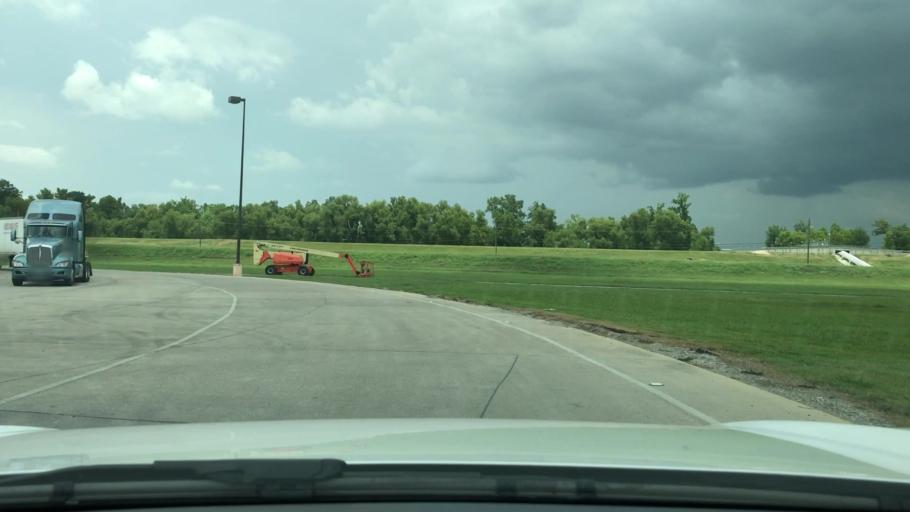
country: US
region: Louisiana
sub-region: Iberville Parish
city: Saint Gabriel
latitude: 30.2687
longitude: -91.1436
